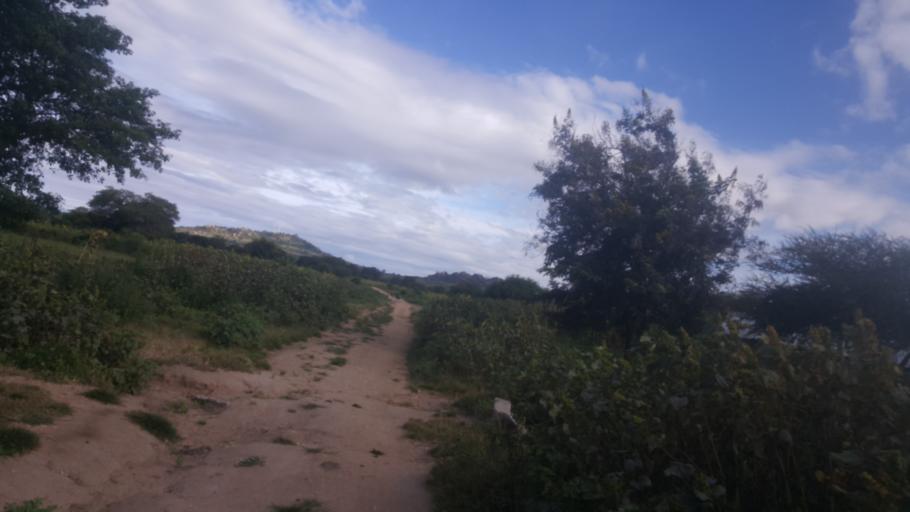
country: TZ
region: Dodoma
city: Dodoma
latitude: -6.0885
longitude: 35.5245
